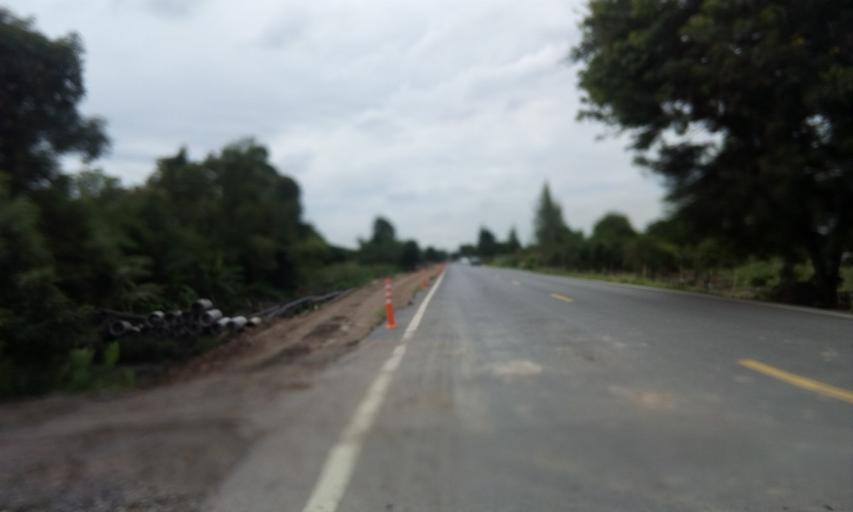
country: TH
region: Nakhon Nayok
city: Ongkharak
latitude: 14.0867
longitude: 100.9144
